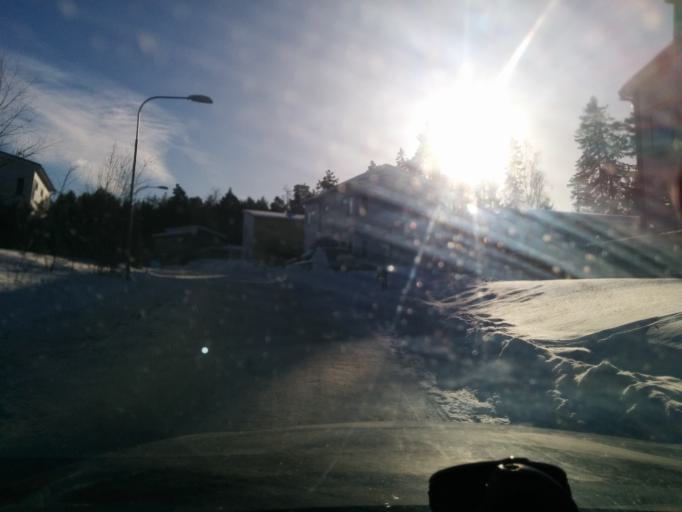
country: SE
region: Stockholm
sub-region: Vallentuna Kommun
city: Vallentuna
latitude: 59.4963
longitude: 18.0785
